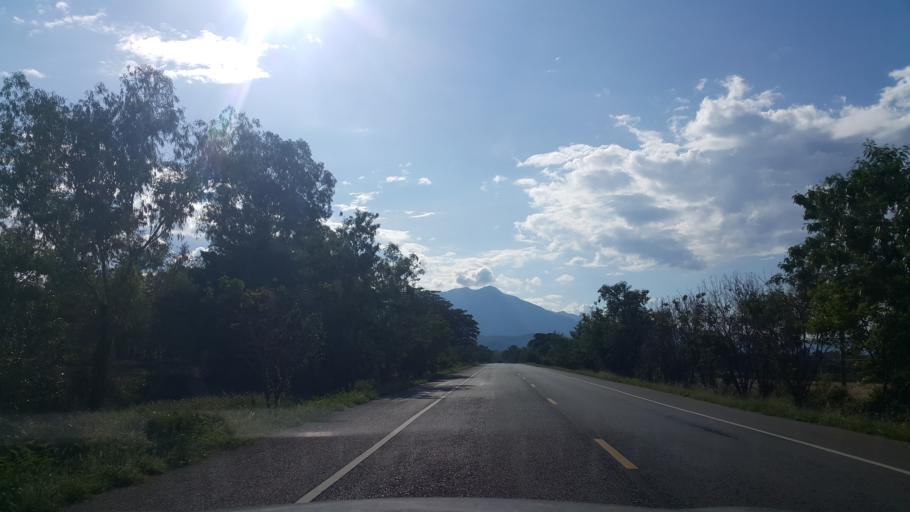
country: TH
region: Phayao
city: Phayao
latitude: 19.0837
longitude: 99.8580
